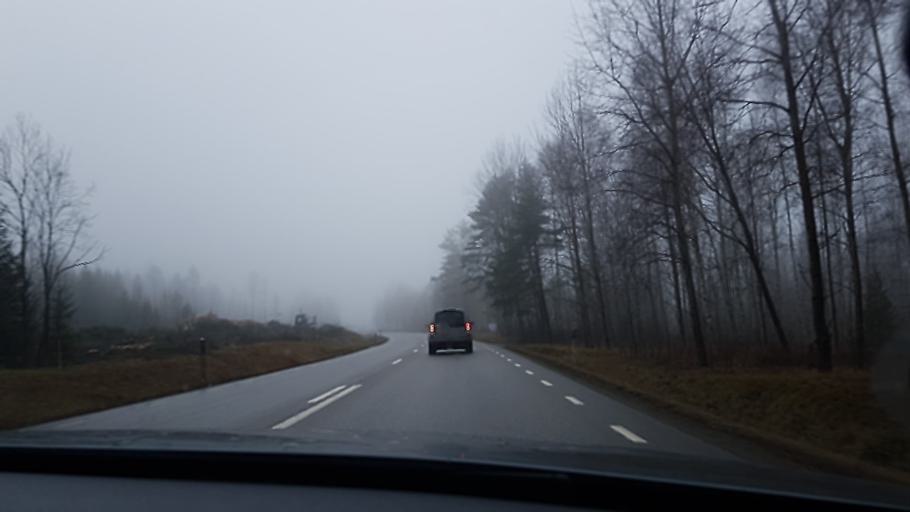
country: SE
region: Vaestra Goetaland
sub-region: Gullspangs Kommun
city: Gullspang
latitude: 58.9674
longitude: 14.0663
